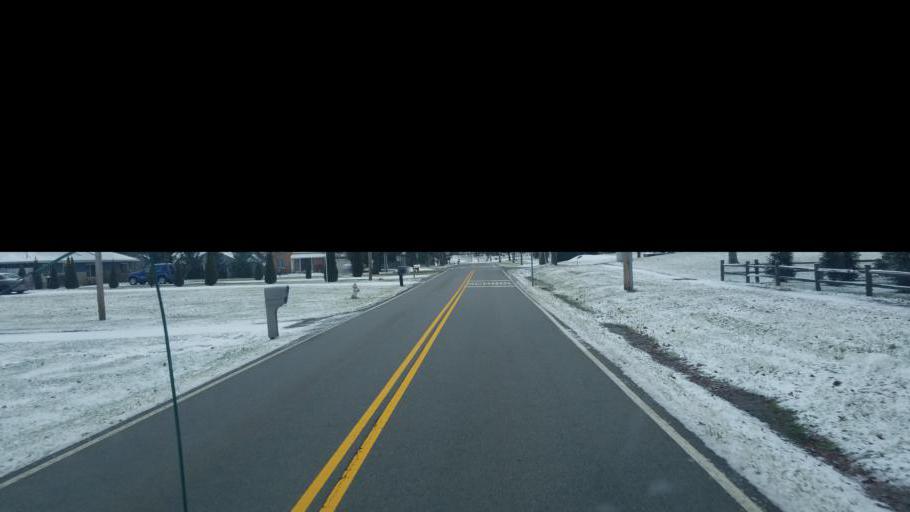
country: US
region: Ohio
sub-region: Franklin County
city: Gahanna
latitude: 40.0334
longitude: -82.8588
